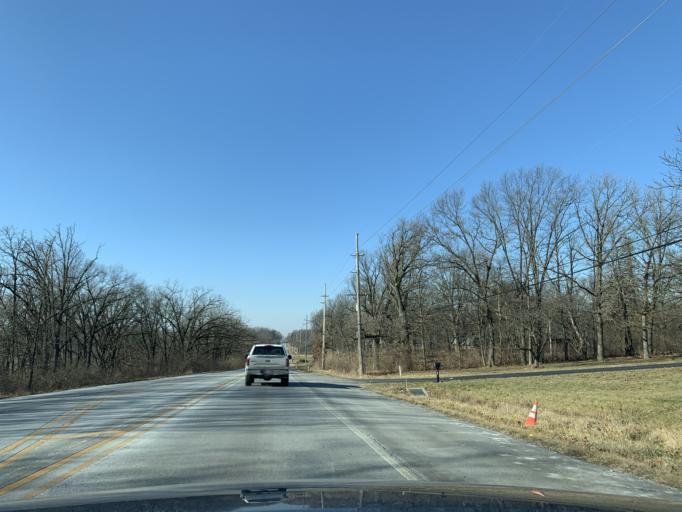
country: US
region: Indiana
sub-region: Lake County
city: Crown Point
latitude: 41.4205
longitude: -87.3895
